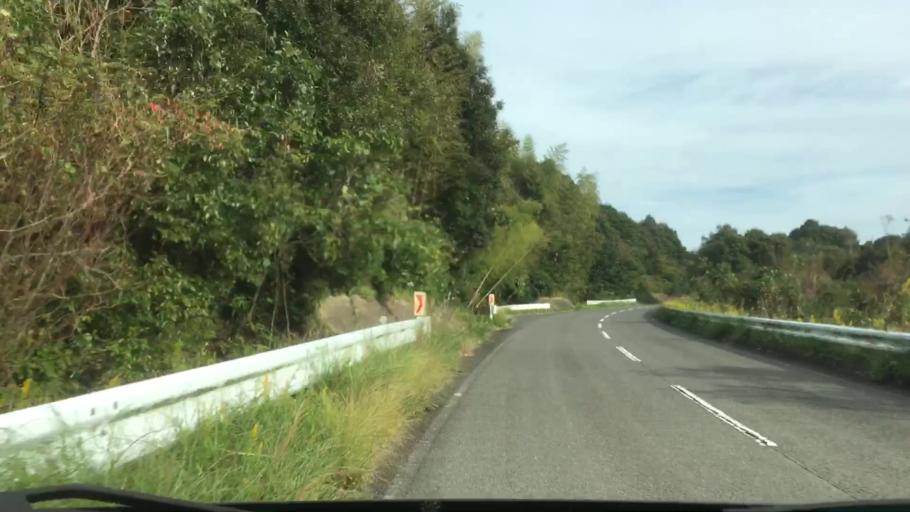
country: JP
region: Nagasaki
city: Sasebo
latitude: 33.0109
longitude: 129.7061
